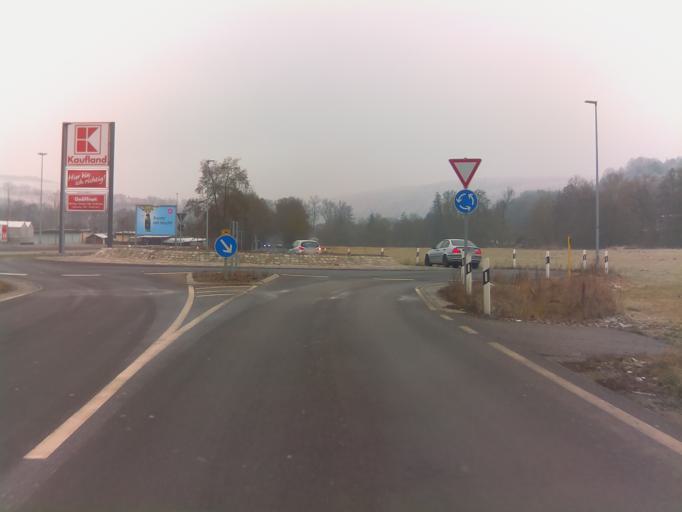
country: DE
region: Thuringia
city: Meiningen
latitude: 50.5587
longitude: 10.4122
